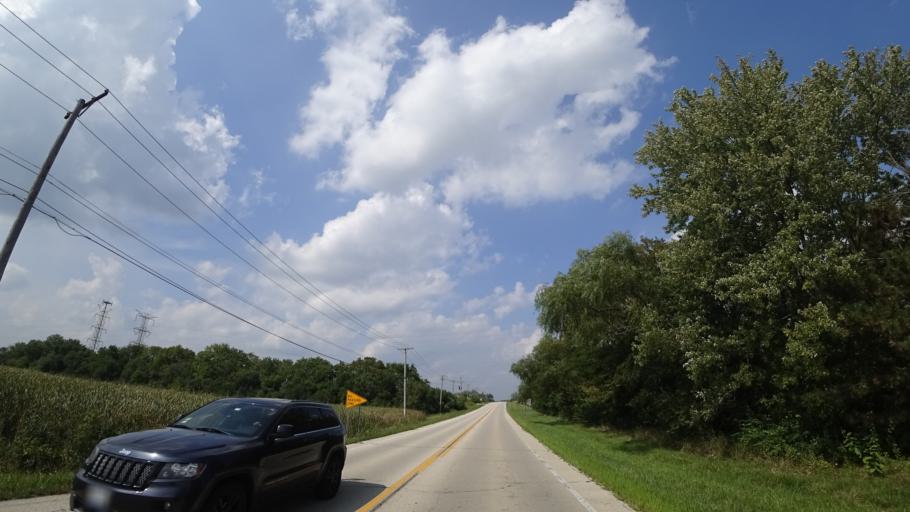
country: US
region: Illinois
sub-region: Will County
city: Goodings Grove
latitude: 41.6395
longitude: -87.8926
